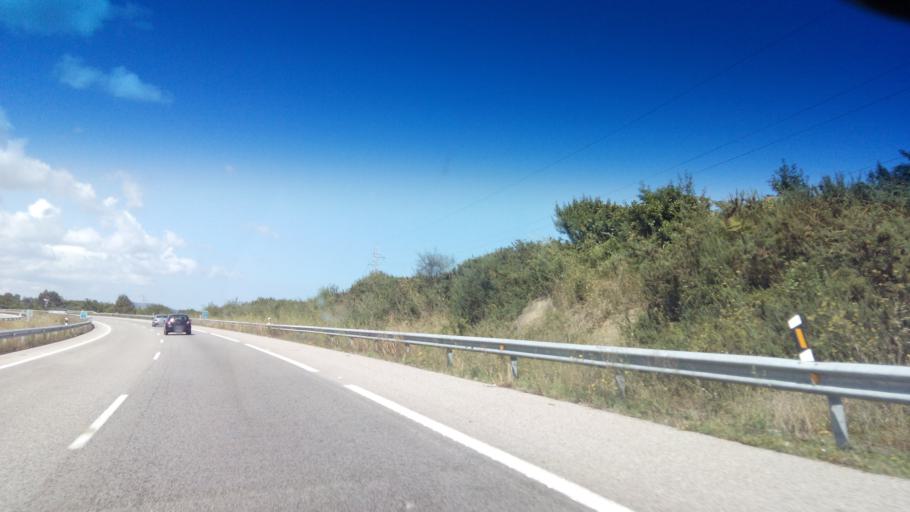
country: ES
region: Asturias
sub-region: Province of Asturias
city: Colunga
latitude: 43.4727
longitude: -5.2212
